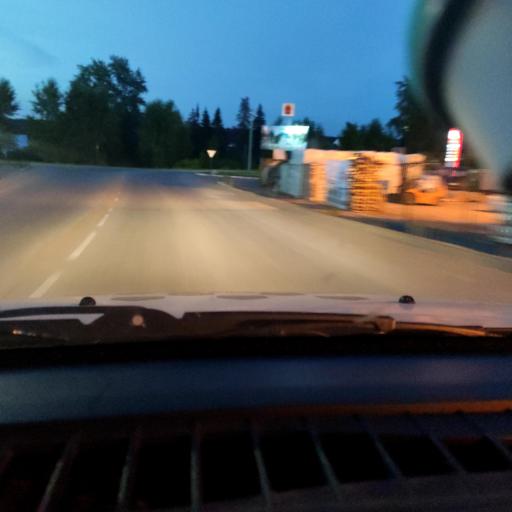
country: RU
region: Perm
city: Polazna
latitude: 58.2873
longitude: 56.4090
